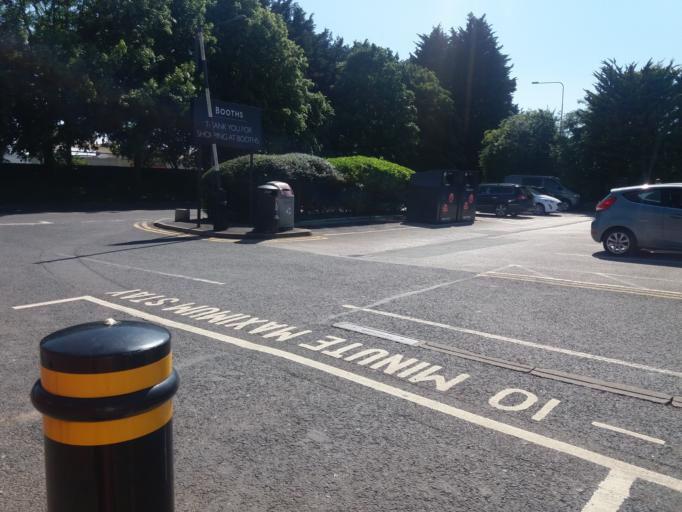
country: GB
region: England
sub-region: Lancashire
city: Preston
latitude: 53.7923
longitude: -2.7067
